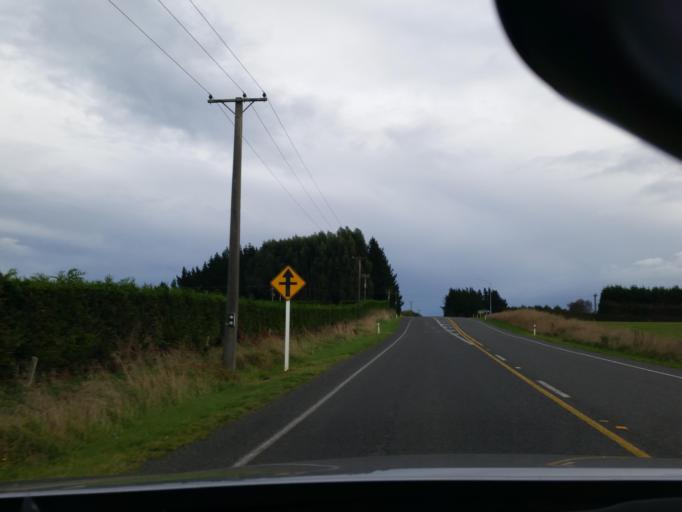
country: NZ
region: Southland
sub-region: Invercargill City
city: Invercargill
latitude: -46.3192
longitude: 168.2494
